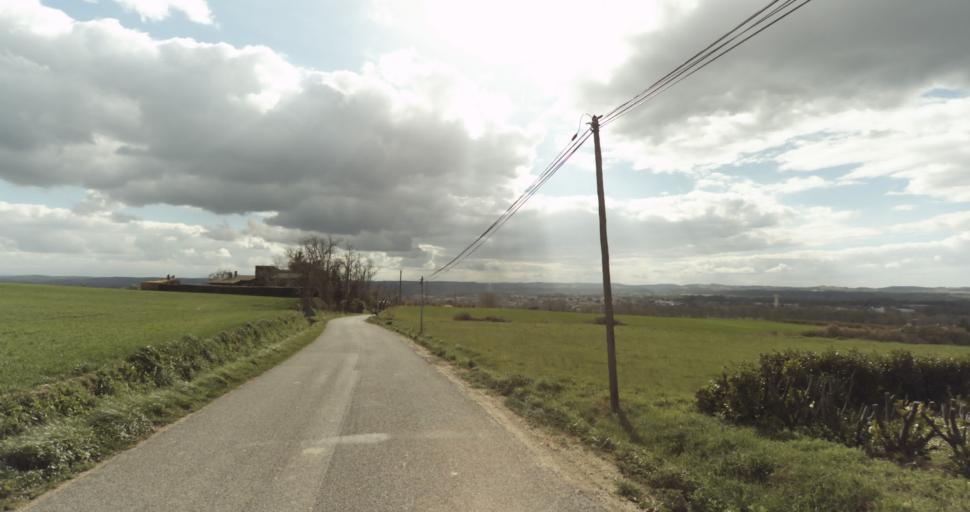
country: FR
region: Midi-Pyrenees
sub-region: Departement de la Haute-Garonne
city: Auterive
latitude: 43.3638
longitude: 1.4820
